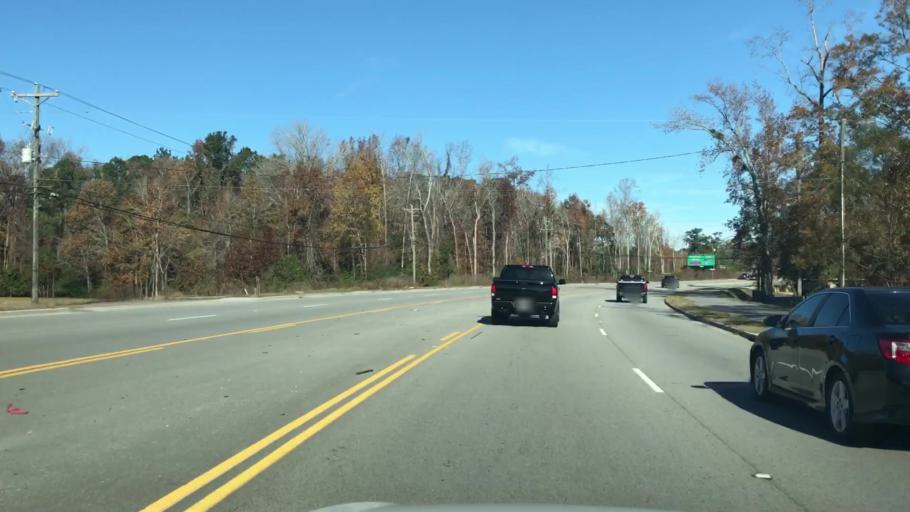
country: US
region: South Carolina
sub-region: Dorchester County
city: Centerville
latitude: 32.9640
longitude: -80.2021
